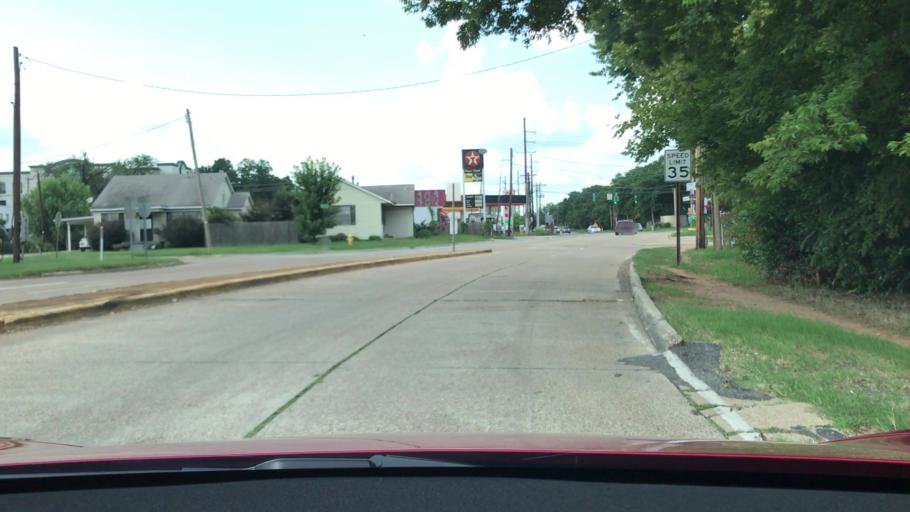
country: US
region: Louisiana
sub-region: Bossier Parish
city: Bossier City
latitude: 32.5145
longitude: -93.7264
